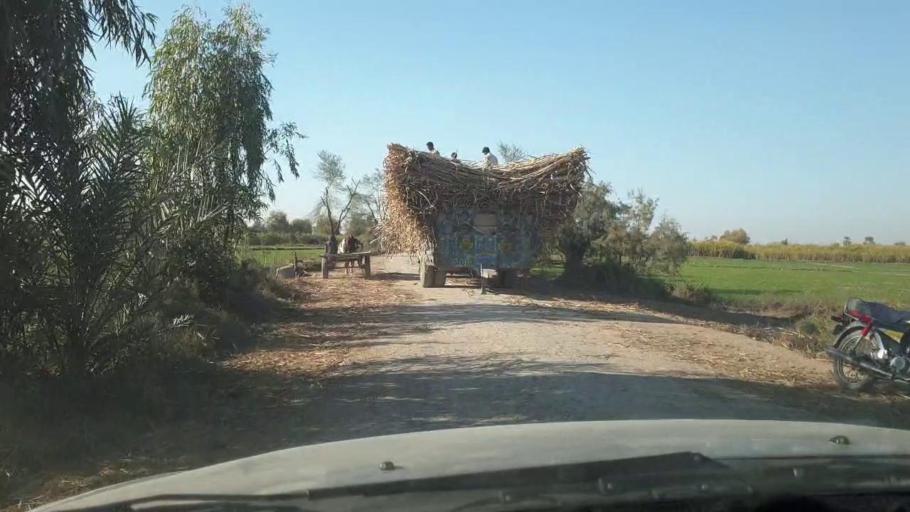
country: PK
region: Sindh
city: Ghotki
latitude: 28.0440
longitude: 69.2941
